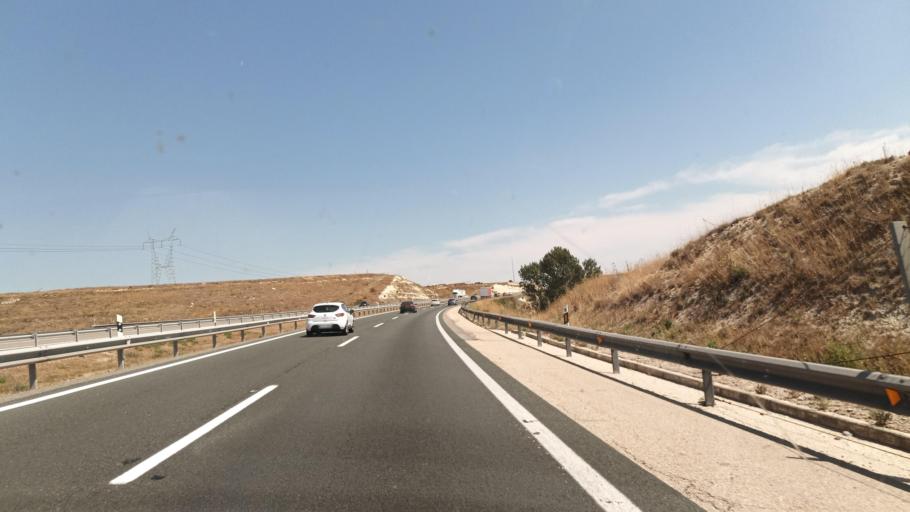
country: ES
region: Castille and Leon
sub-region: Provincia de Burgos
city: Quintanapalla
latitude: 42.4218
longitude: -3.5181
